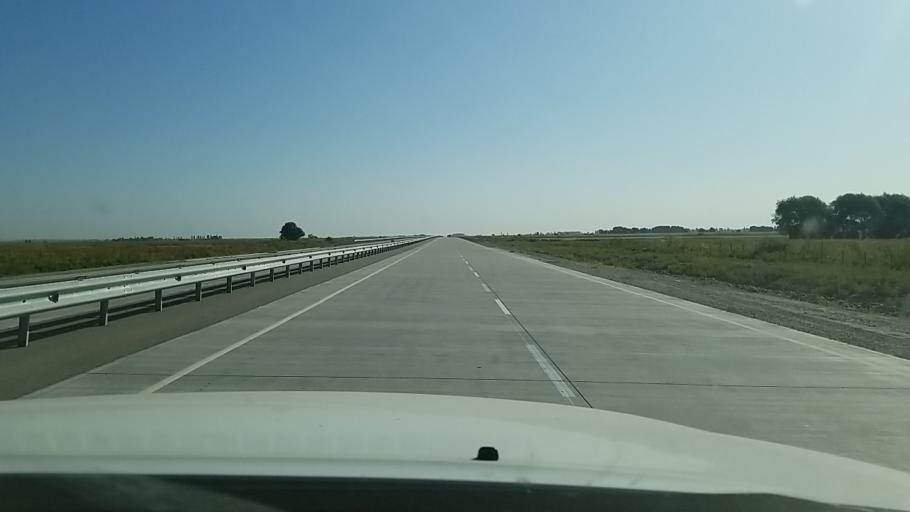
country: KZ
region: Almaty Oblysy
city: Turgen'
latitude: 43.5555
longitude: 77.7983
